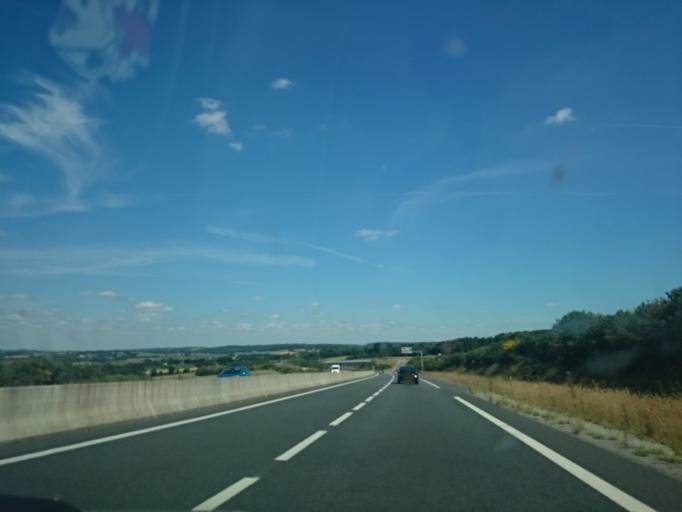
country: FR
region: Brittany
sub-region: Departement des Cotes-d'Armor
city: Gouarec
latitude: 48.2350
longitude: -3.2125
